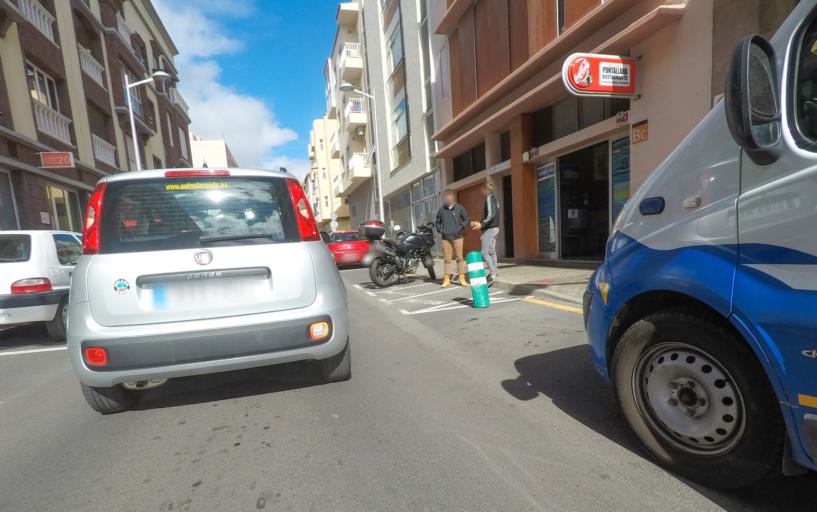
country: ES
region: Canary Islands
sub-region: Provincia de Santa Cruz de Tenerife
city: San Sebastian de la Gomera
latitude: 28.0934
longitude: -17.1139
